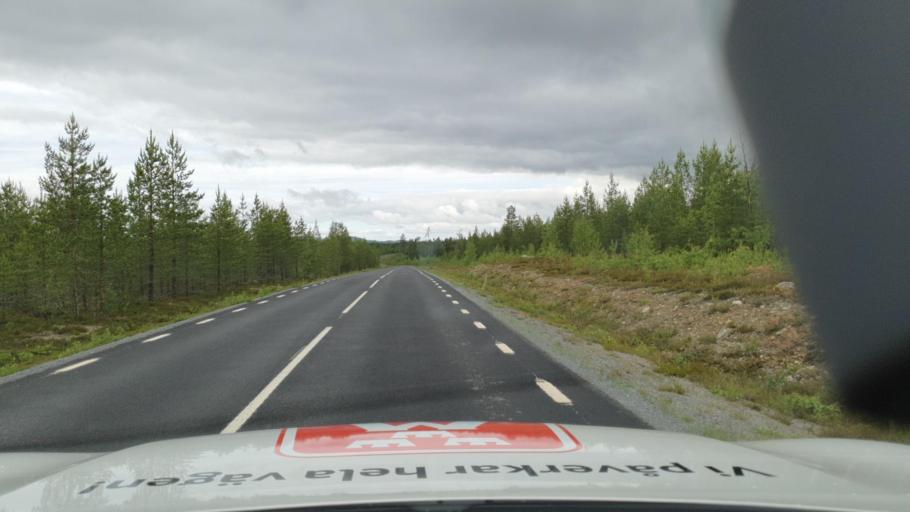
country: SE
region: Vaesterbotten
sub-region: Dorotea Kommun
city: Dorotea
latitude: 64.1923
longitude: 16.5901
